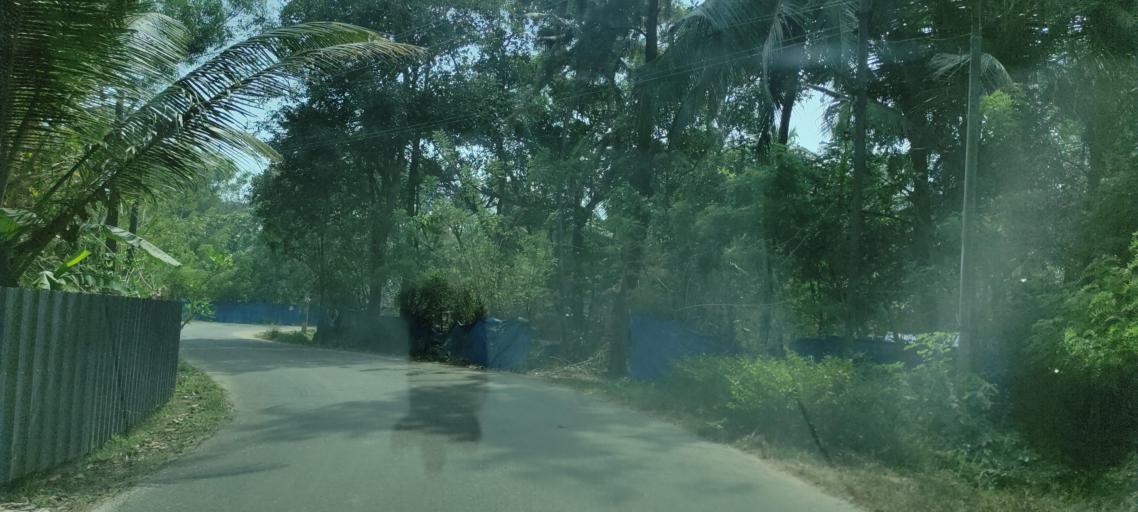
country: IN
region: Kerala
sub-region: Alappuzha
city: Shertallai
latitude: 9.6246
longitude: 76.3500
